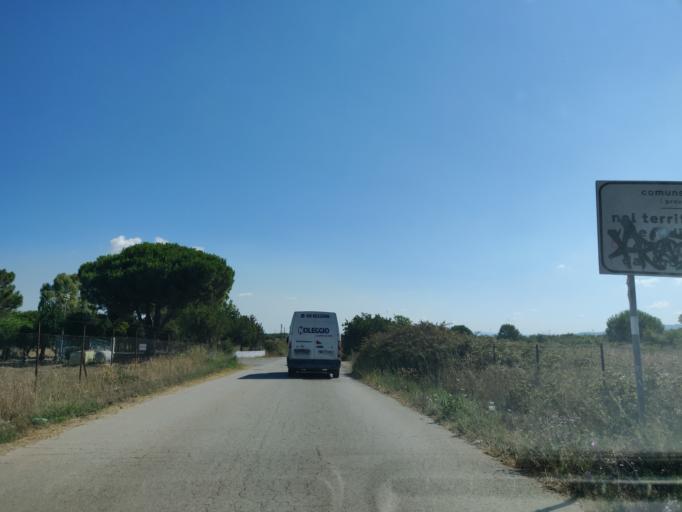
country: IT
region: Latium
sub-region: Citta metropolitana di Roma Capitale
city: Aurelia
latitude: 42.1661
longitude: 11.7422
